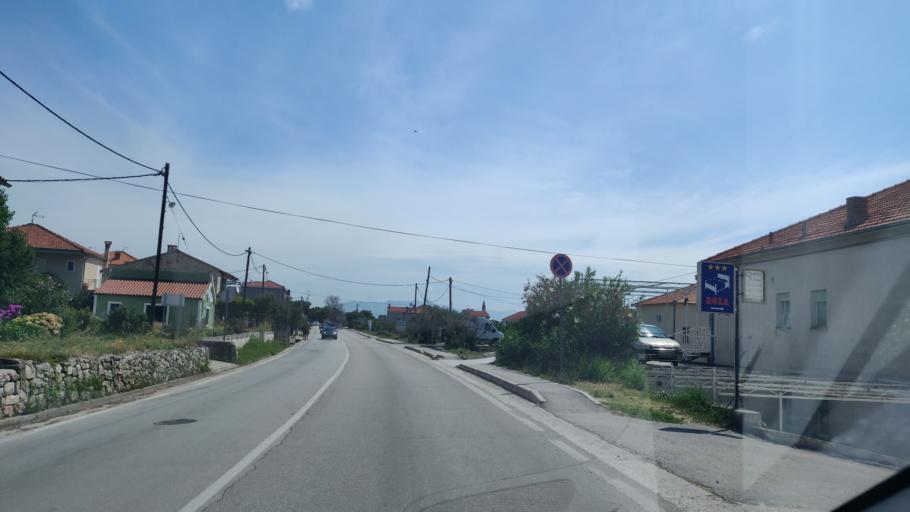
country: HR
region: Splitsko-Dalmatinska
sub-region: Grad Trogir
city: Trogir
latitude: 43.5174
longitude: 16.2393
